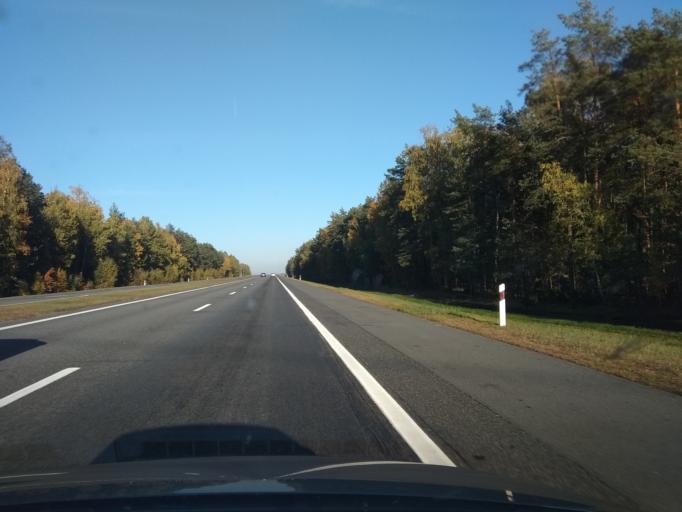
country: BY
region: Brest
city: Nyakhachava
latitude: 52.6554
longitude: 25.2651
